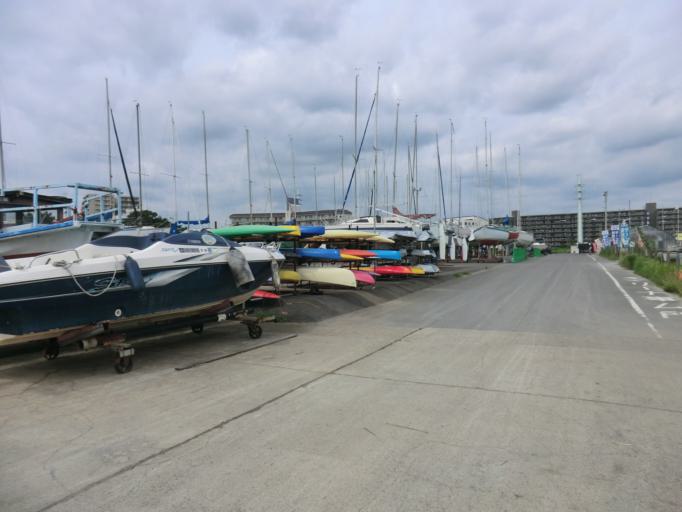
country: JP
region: Ibaraki
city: Ami
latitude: 36.0822
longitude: 140.2140
